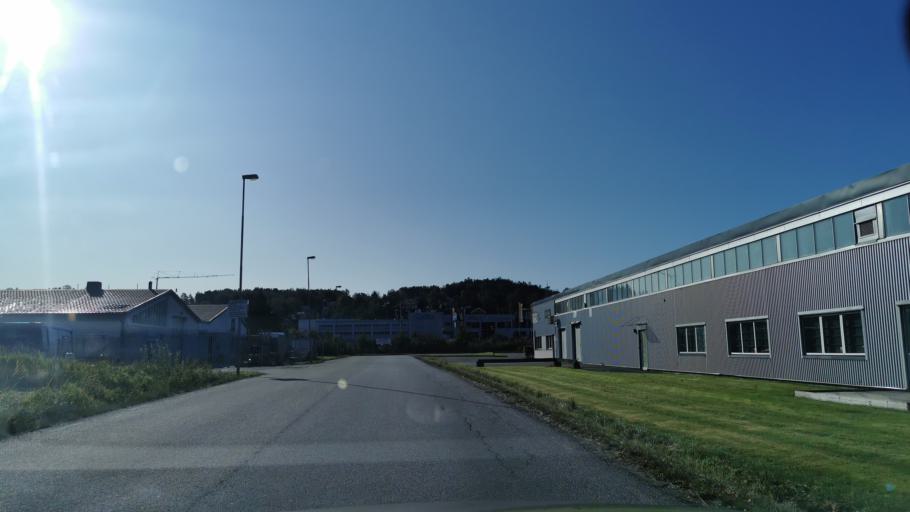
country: SE
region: Vaestra Goetaland
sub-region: Partille Kommun
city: Partille
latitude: 57.7339
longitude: 12.0648
